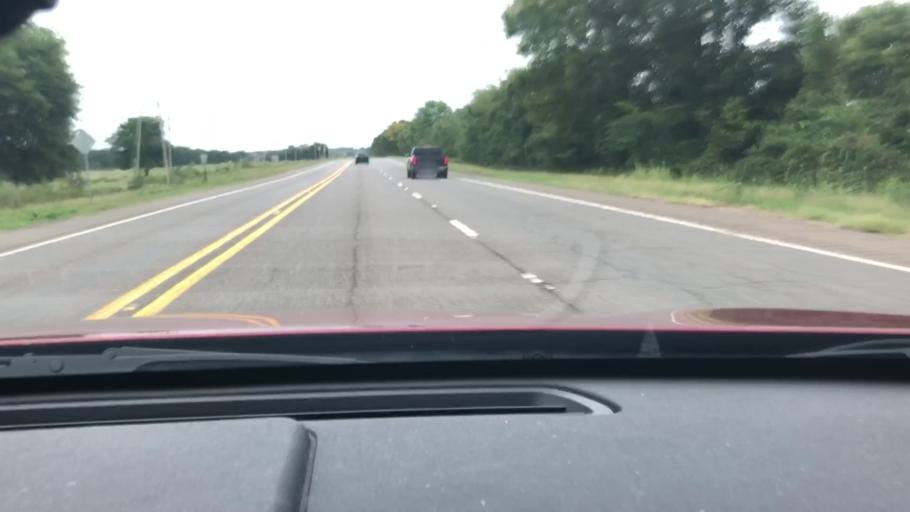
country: US
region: Arkansas
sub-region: Lafayette County
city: Lewisville
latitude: 33.3558
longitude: -93.6594
